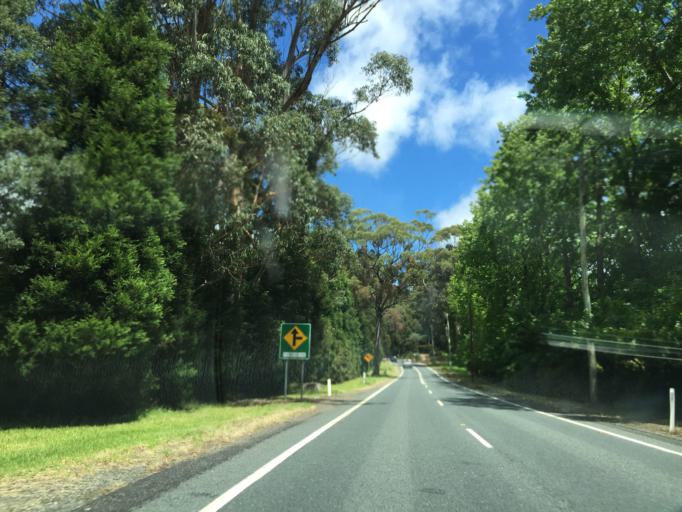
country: AU
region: New South Wales
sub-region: Blue Mountains Municipality
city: Lawson
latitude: -33.5166
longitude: 150.4695
